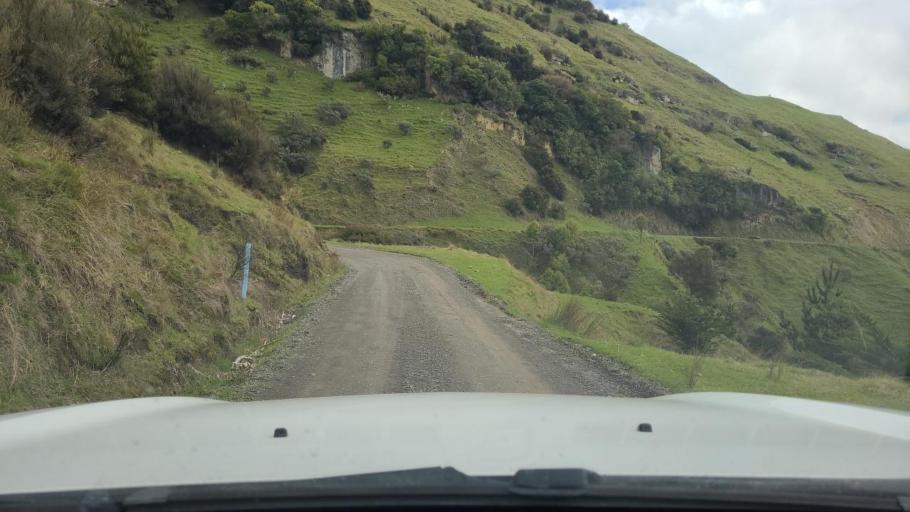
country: NZ
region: Wellington
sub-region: South Wairarapa District
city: Waipawa
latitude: -41.3668
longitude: 175.3940
